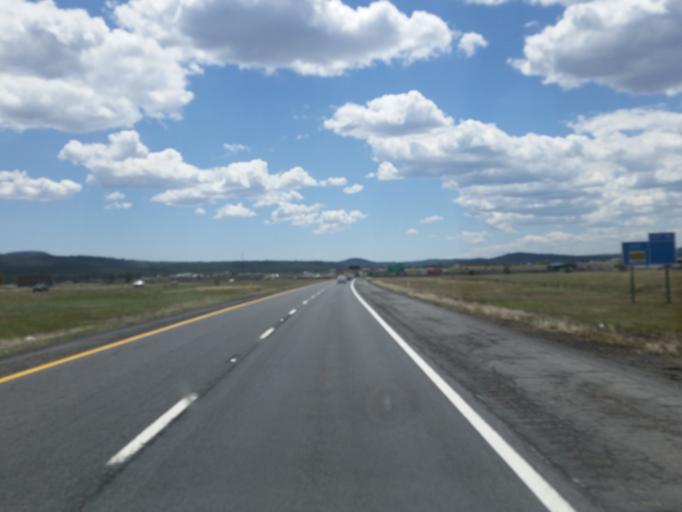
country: US
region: Arizona
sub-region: Coconino County
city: Parks
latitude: 35.2430
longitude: -111.8379
